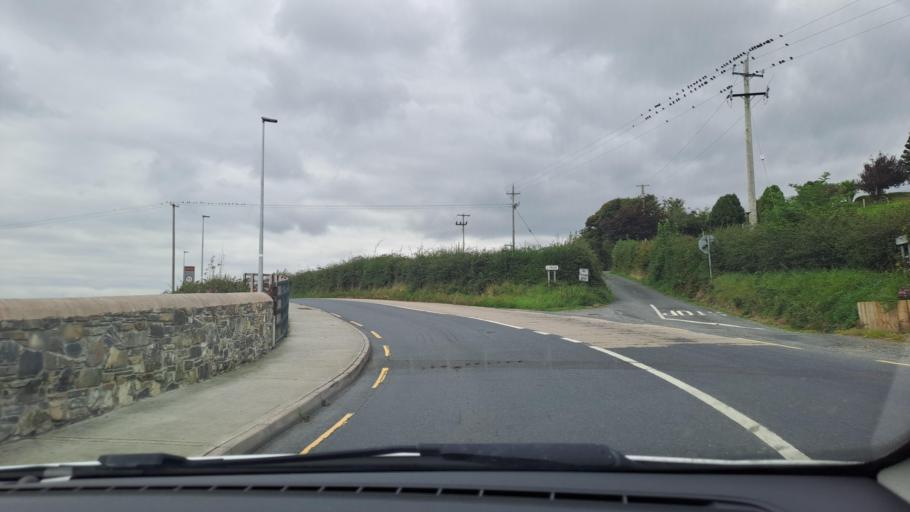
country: IE
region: Ulster
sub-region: An Cabhan
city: Bailieborough
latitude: 53.9978
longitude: -6.8982
